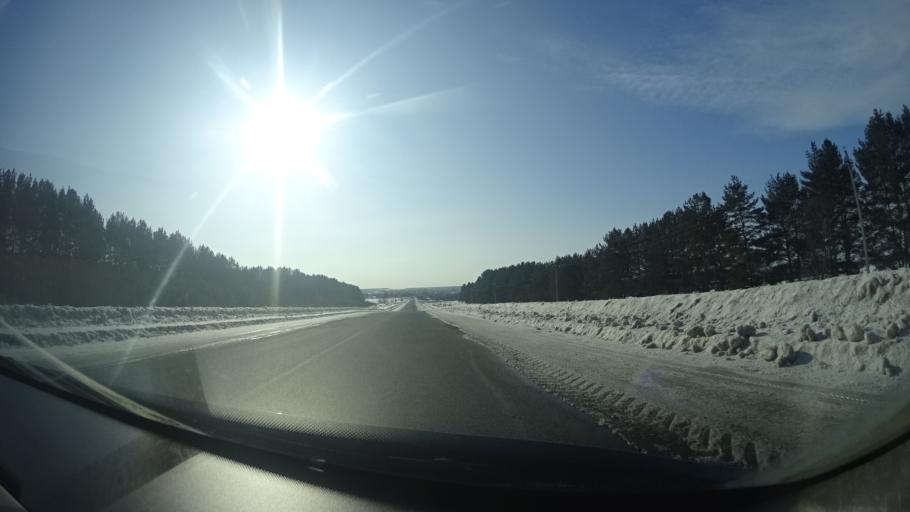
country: RU
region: Perm
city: Kuyeda
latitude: 56.4673
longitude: 55.5908
